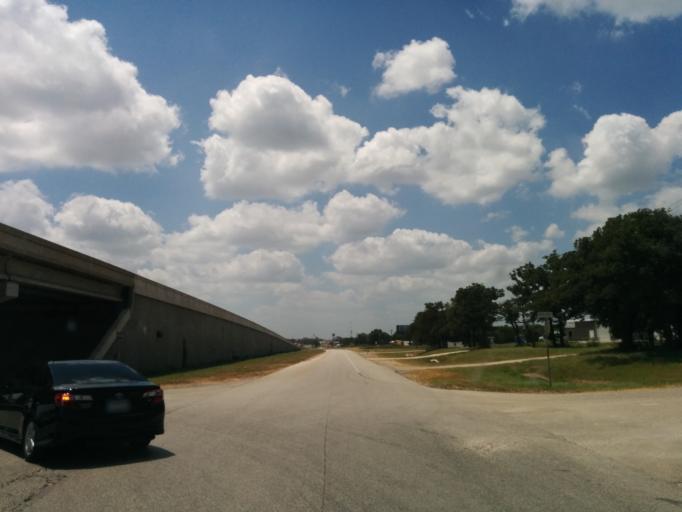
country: US
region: Texas
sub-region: Bastrop County
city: Wyldwood
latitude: 30.1126
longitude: -97.4149
